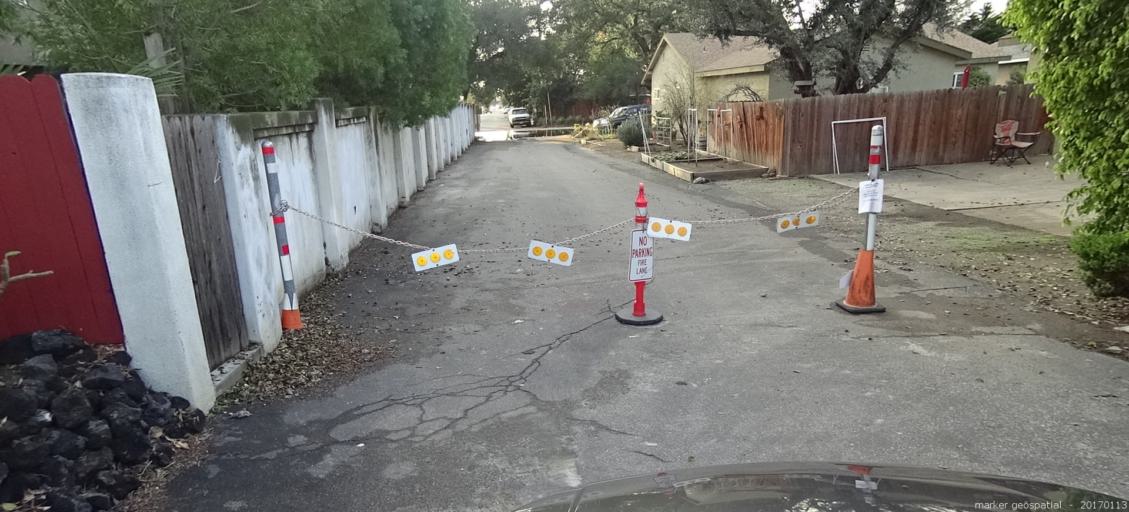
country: US
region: California
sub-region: Orange County
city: Villa Park
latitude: 33.8130
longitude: -117.7801
